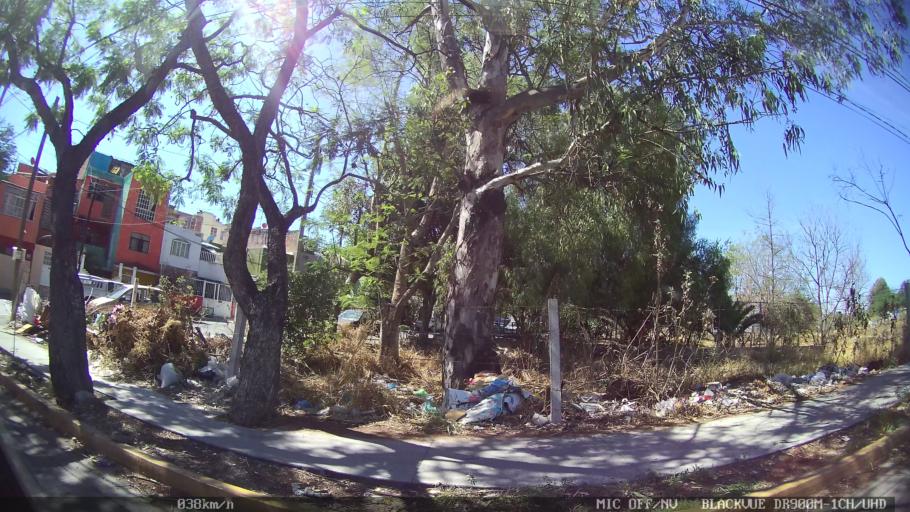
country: MX
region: Jalisco
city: Tlaquepaque
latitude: 20.7021
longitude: -103.2849
